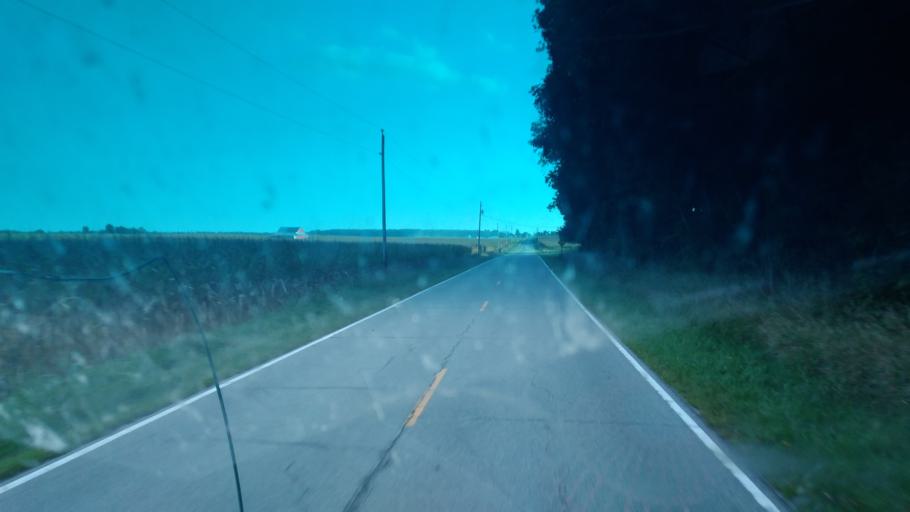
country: US
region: Ohio
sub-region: Crawford County
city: Bucyrus
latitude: 40.9029
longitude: -82.9018
